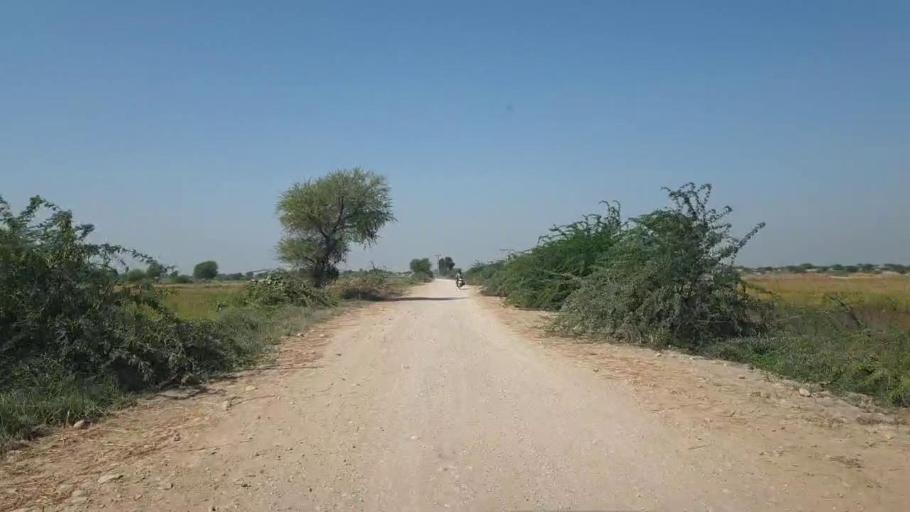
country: PK
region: Sindh
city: Talhar
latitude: 24.8338
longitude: 68.8025
